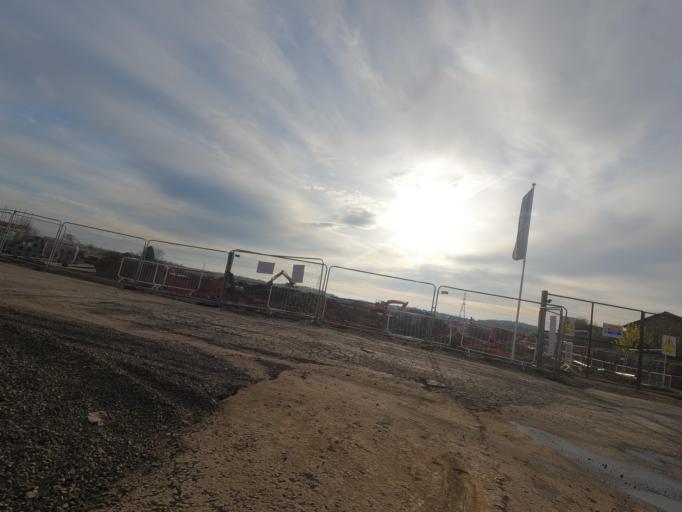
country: GB
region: England
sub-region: Northumberland
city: Cramlington
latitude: 55.0842
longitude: -1.6130
